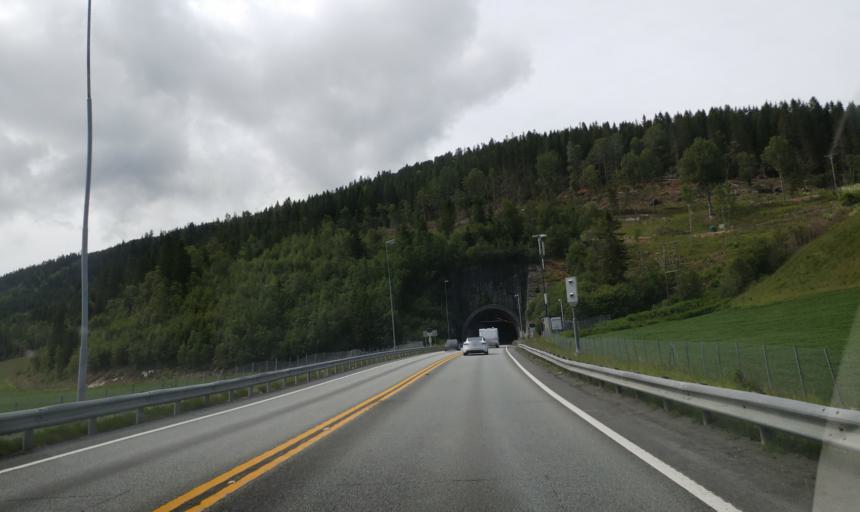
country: NO
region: Sor-Trondelag
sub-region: Malvik
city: Malvik
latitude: 63.4221
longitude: 10.6192
